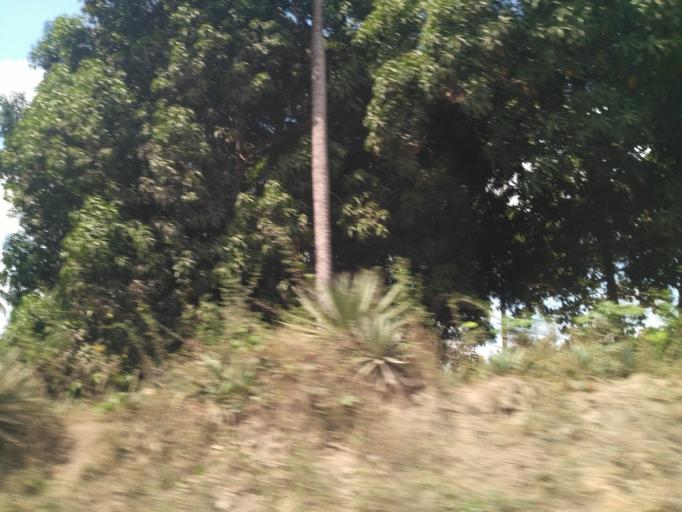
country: TZ
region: Dar es Salaam
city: Dar es Salaam
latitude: -6.8833
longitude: 39.3340
